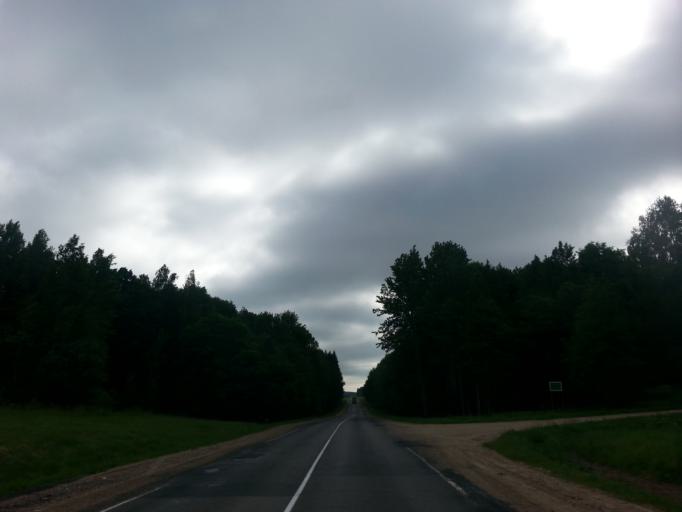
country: BY
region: Vitebsk
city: Mosar
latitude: 55.0634
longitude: 27.2723
